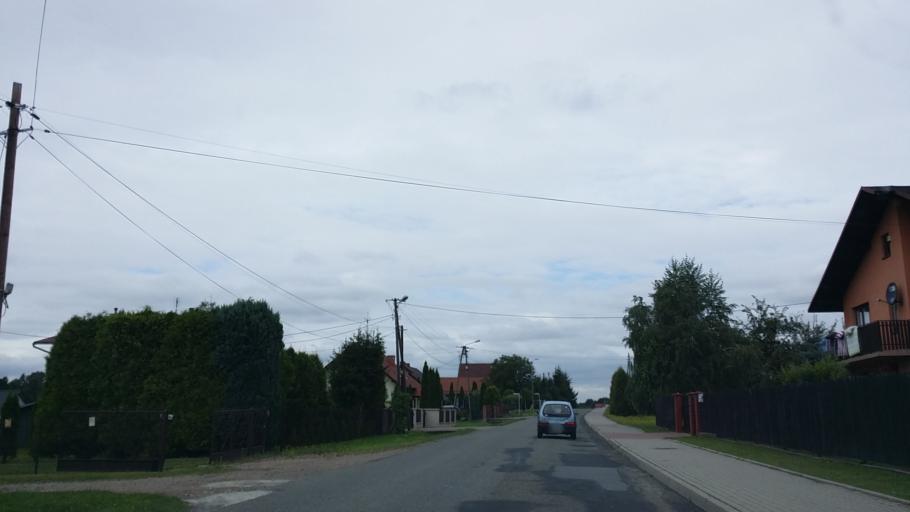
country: PL
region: Lesser Poland Voivodeship
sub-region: Powiat wadowicki
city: Tomice
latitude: 49.8992
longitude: 19.4655
